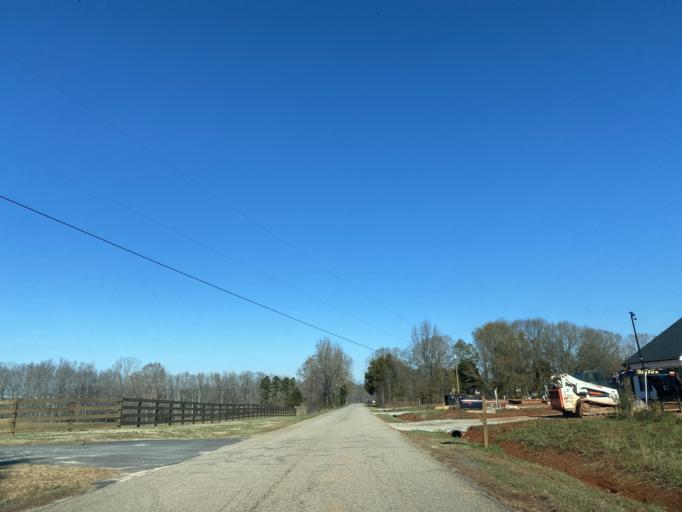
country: US
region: South Carolina
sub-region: Spartanburg County
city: Mayo
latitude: 35.1368
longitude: -81.7861
